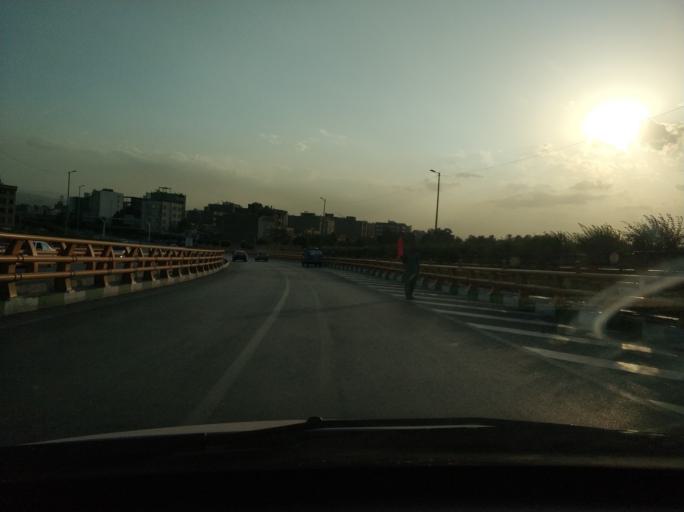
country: IR
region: Razavi Khorasan
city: Mashhad
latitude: 36.3402
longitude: 59.5456
